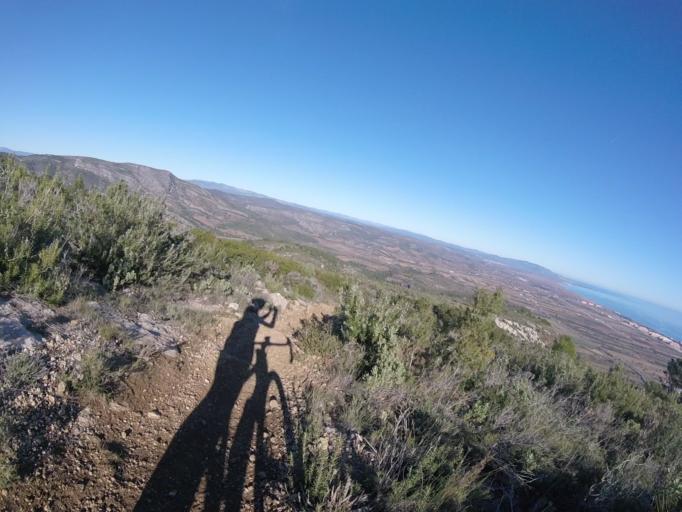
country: ES
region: Valencia
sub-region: Provincia de Castello
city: Orpesa/Oropesa del Mar
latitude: 40.1019
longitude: 0.1127
